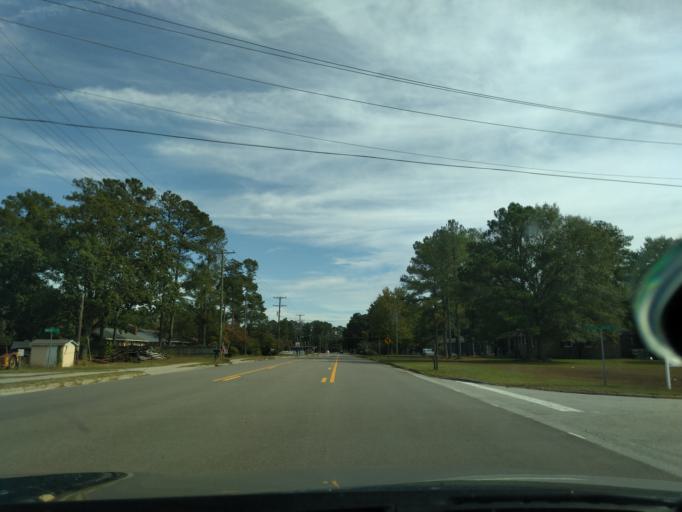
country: US
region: North Carolina
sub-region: Beaufort County
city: River Road
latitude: 35.5051
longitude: -76.9907
